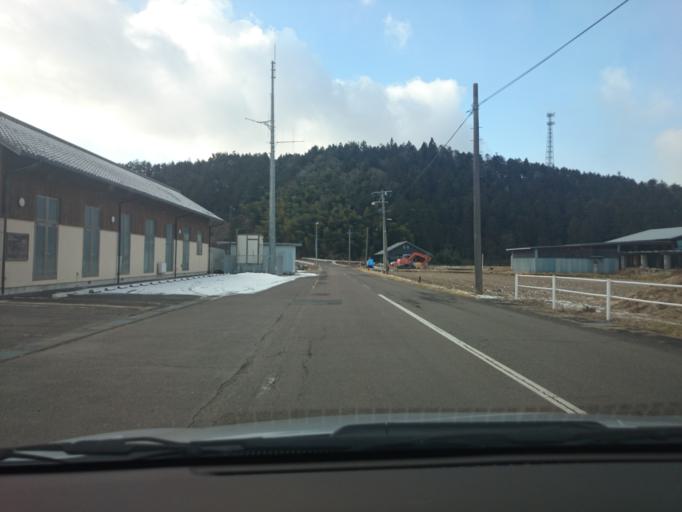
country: JP
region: Gifu
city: Nakatsugawa
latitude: 35.7520
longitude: 137.3333
